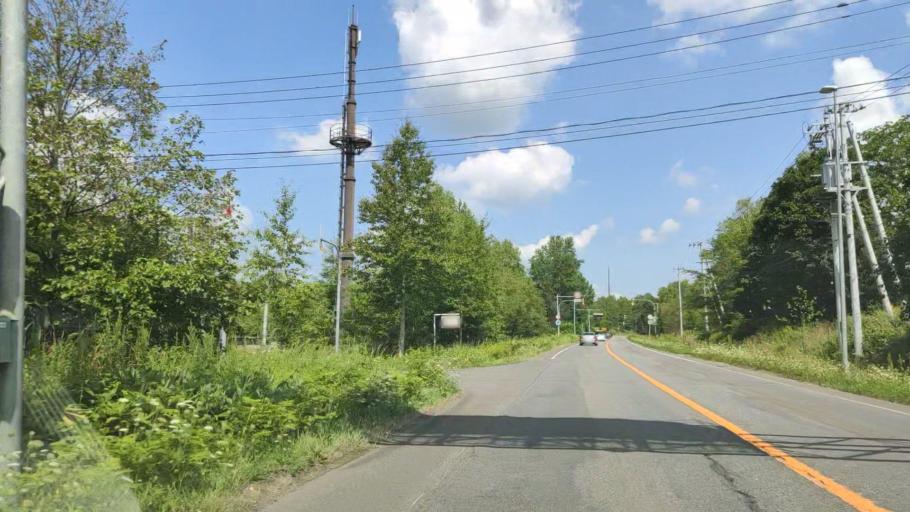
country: JP
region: Hokkaido
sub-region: Asahikawa-shi
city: Asahikawa
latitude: 43.5797
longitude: 142.4381
